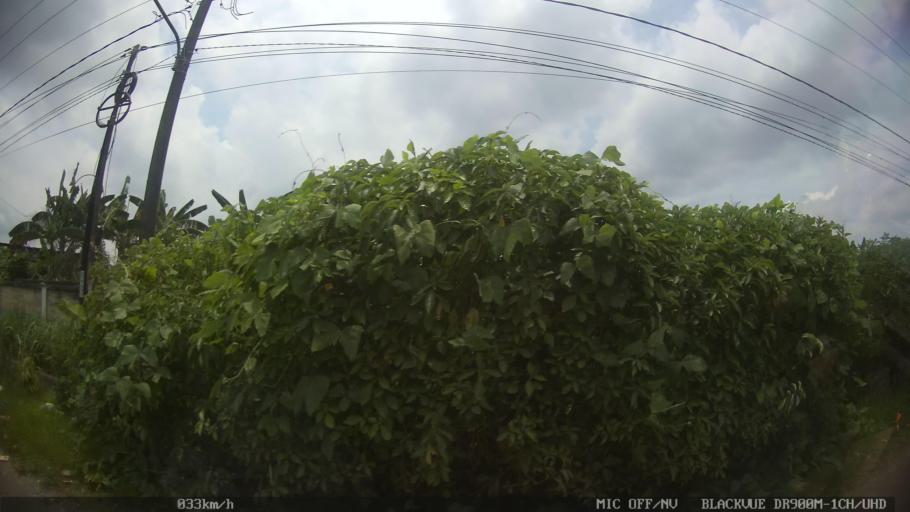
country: ID
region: North Sumatra
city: Labuhan Deli
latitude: 3.6815
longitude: 98.6697
